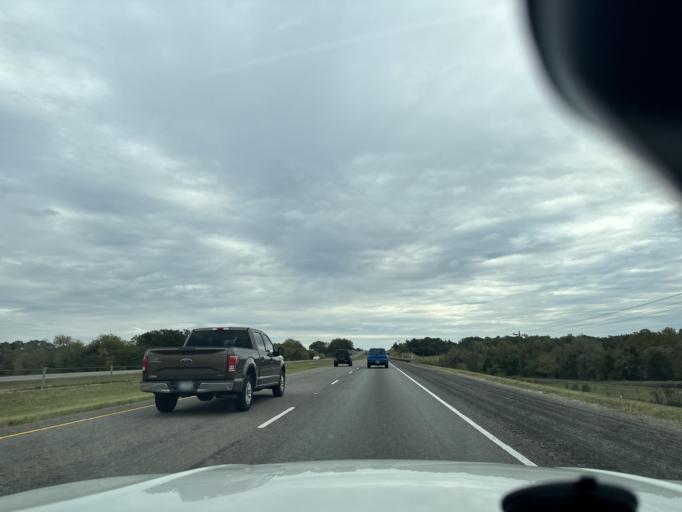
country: US
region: Texas
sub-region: Washington County
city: Brenham
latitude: 30.1878
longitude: -96.5034
